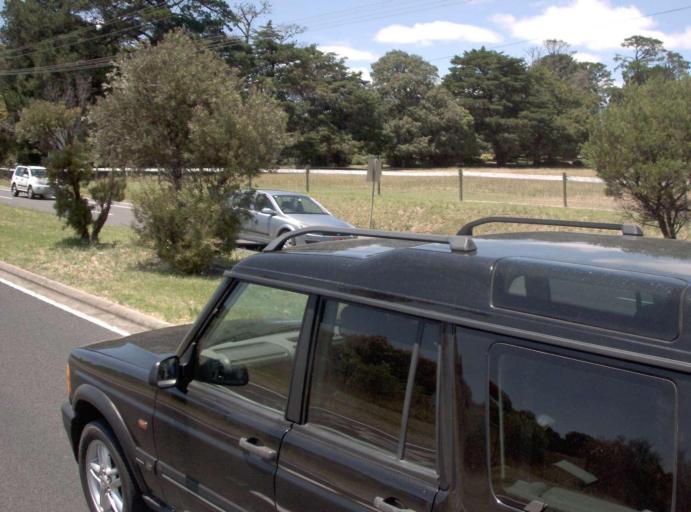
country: AU
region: Victoria
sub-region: Mornington Peninsula
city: Mornington
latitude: -38.2122
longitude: 145.0670
